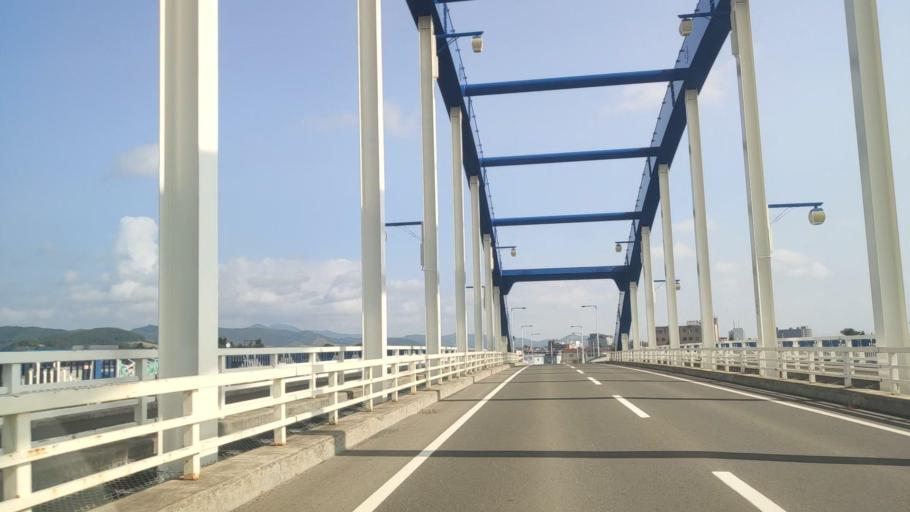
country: JP
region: Hokkaido
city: Shimo-furano
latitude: 43.3379
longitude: 142.3847
